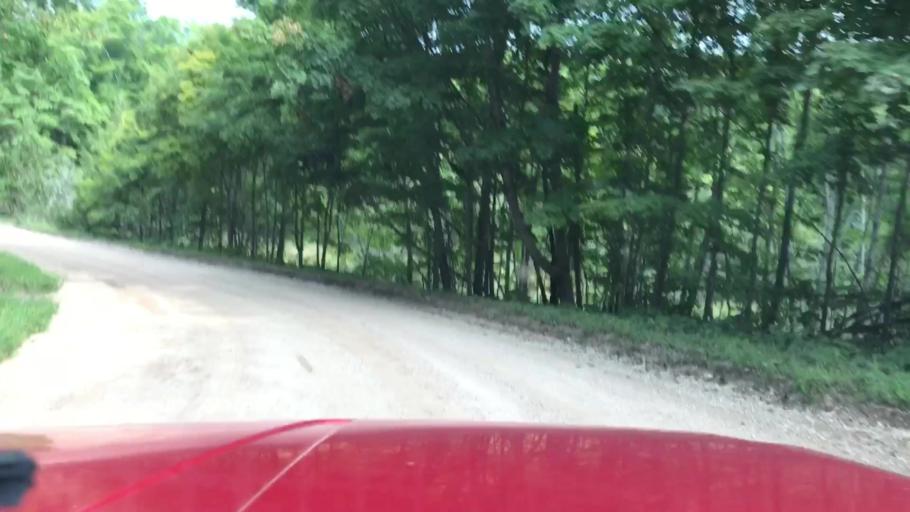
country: US
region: Michigan
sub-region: Charlevoix County
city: Charlevoix
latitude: 45.7419
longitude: -85.5589
